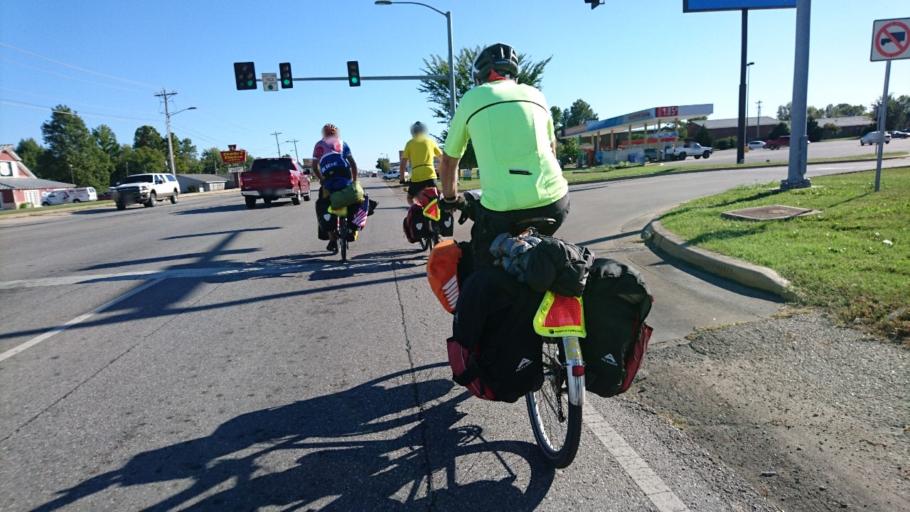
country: US
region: Oklahoma
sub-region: Ottawa County
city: Commerce
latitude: 36.9047
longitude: -94.8776
